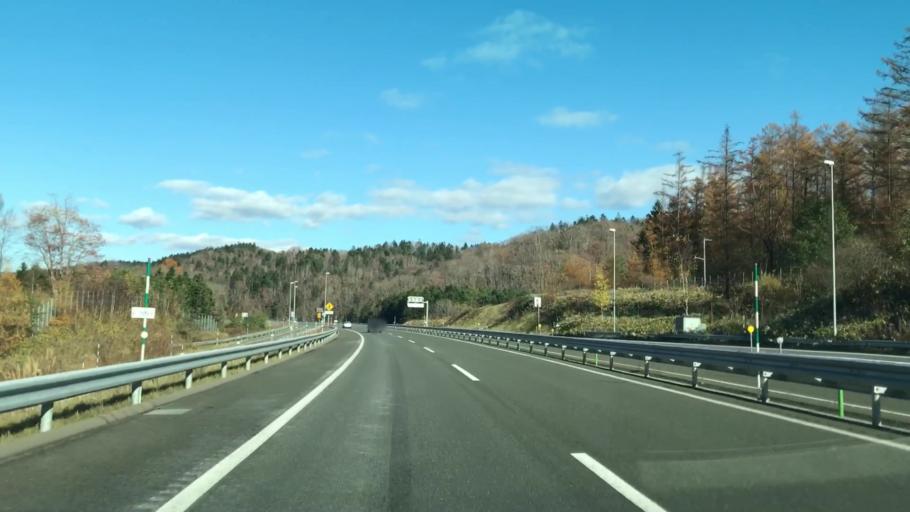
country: JP
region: Hokkaido
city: Shimo-furano
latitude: 42.9197
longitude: 142.1972
